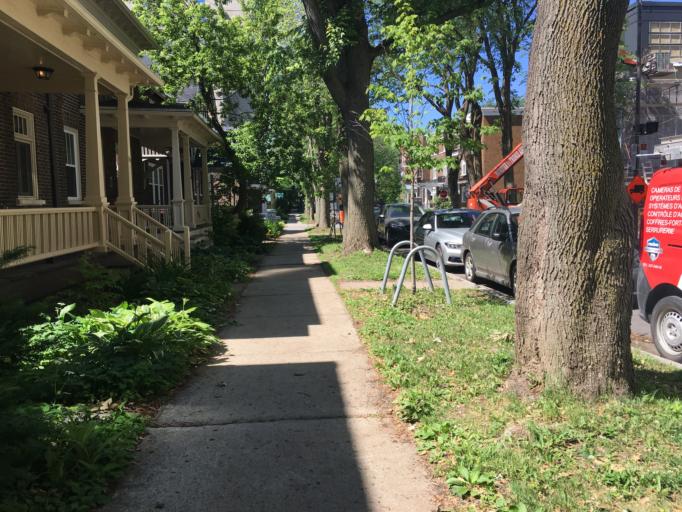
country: CA
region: Quebec
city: Quebec
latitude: 46.8026
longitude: -71.2210
